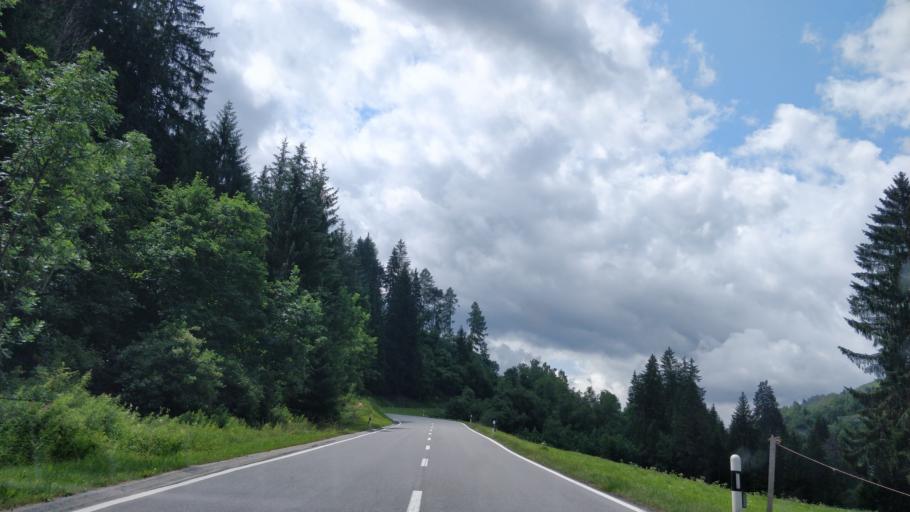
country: CH
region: Grisons
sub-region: Surselva District
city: Ilanz
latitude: 46.7148
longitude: 9.1979
